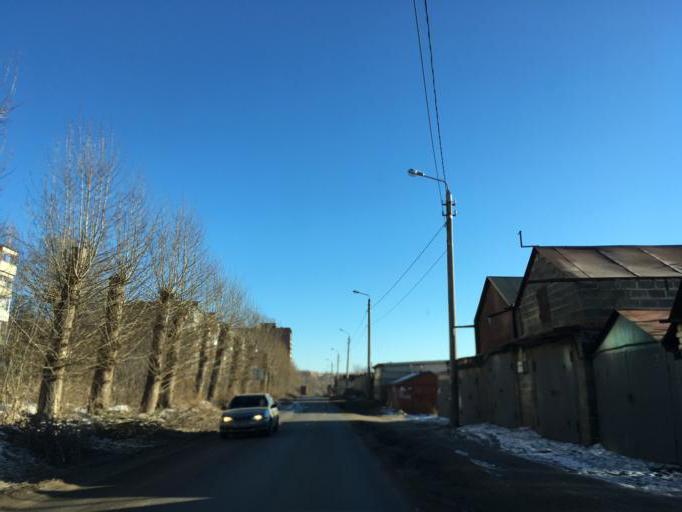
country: RU
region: Tula
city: Tula
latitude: 54.1933
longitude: 37.6700
